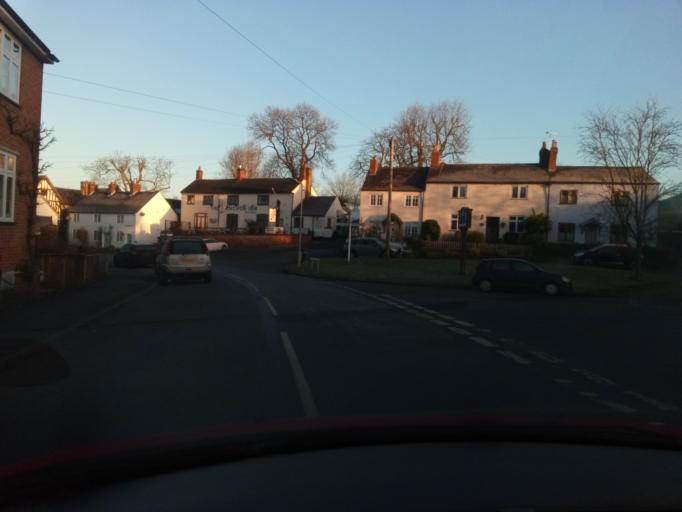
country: GB
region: England
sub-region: Leicestershire
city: Barrow upon Soar
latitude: 52.7723
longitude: -1.1230
